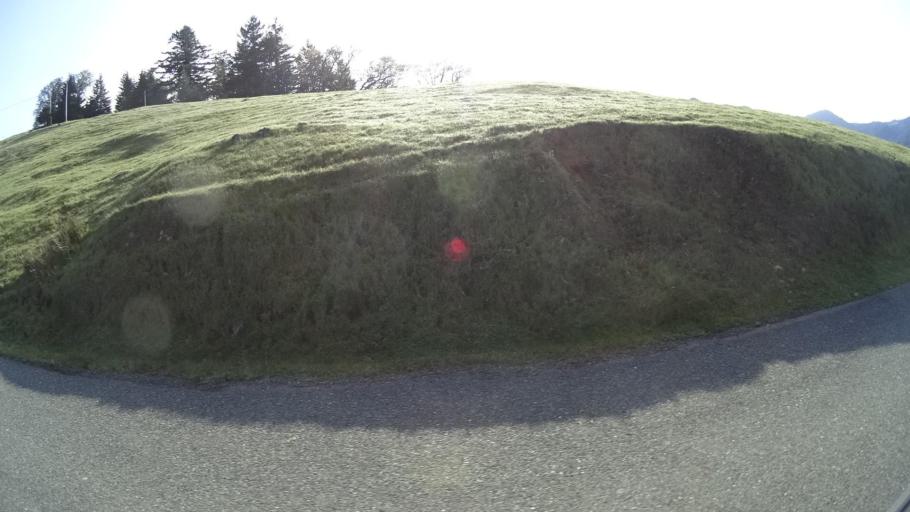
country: US
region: California
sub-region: Humboldt County
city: Blue Lake
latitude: 40.7185
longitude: -123.9424
